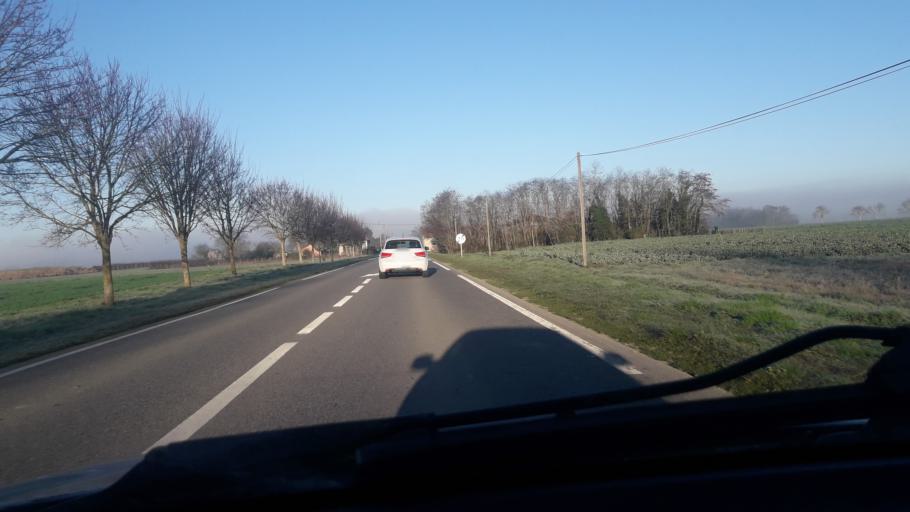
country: FR
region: Midi-Pyrenees
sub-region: Departement de la Haute-Garonne
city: Carbonne
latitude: 43.2974
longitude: 1.1989
